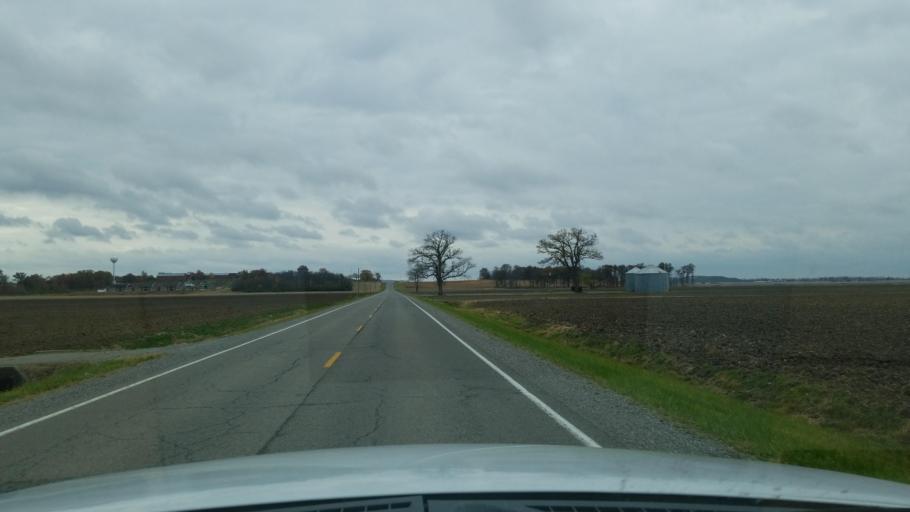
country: US
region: Illinois
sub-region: Saline County
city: Eldorado
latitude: 37.7624
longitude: -88.4383
